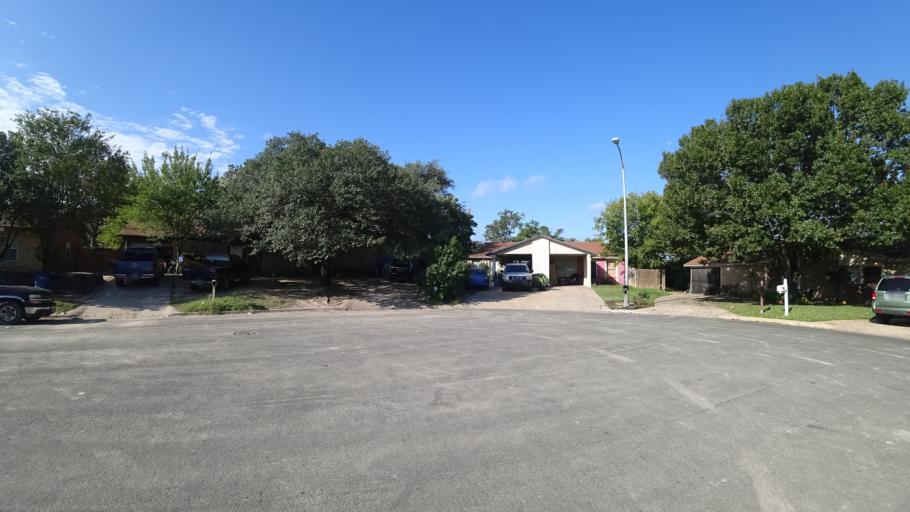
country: US
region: Texas
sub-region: Travis County
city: Austin
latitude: 30.3298
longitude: -97.6922
